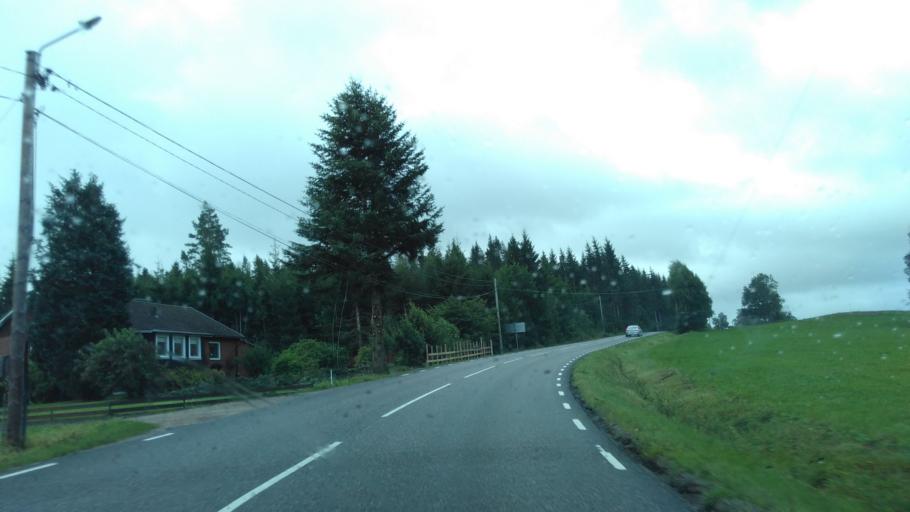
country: SE
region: Vaestra Goetaland
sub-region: Boras Kommun
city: Ganghester
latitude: 57.7868
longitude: 13.0238
